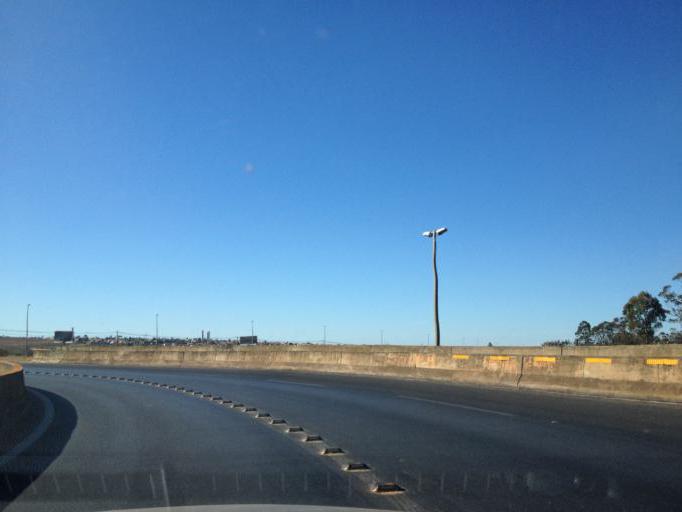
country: BR
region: Federal District
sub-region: Brasilia
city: Brasilia
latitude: -15.6879
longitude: -47.8571
